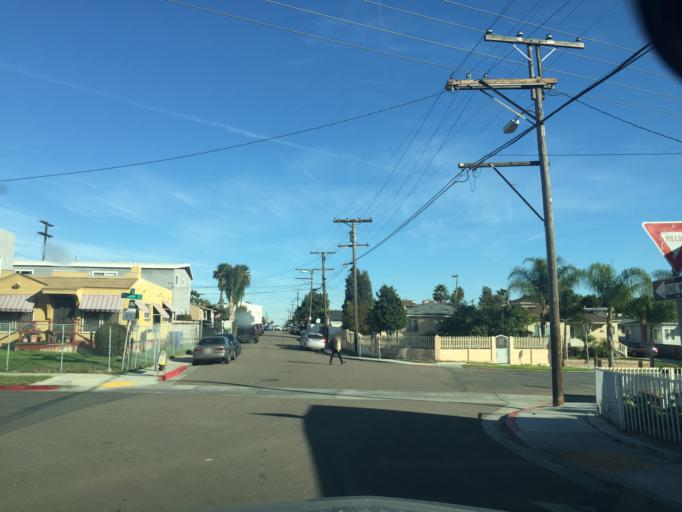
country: US
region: California
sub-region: San Diego County
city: San Diego
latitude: 32.7516
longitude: -117.1218
